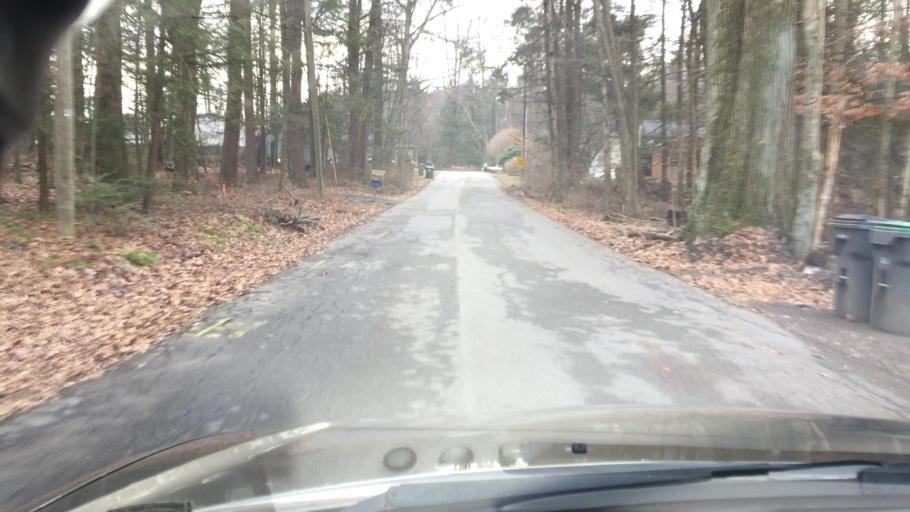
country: US
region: Pennsylvania
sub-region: Luzerne County
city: Harveys Lake
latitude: 41.3749
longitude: -76.0495
